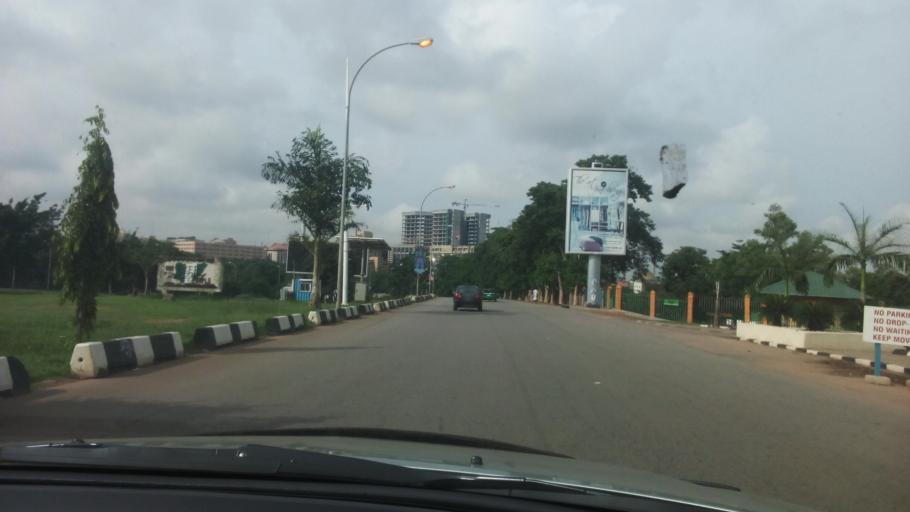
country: NG
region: Abuja Federal Capital Territory
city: Abuja
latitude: 9.0728
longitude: 7.4957
